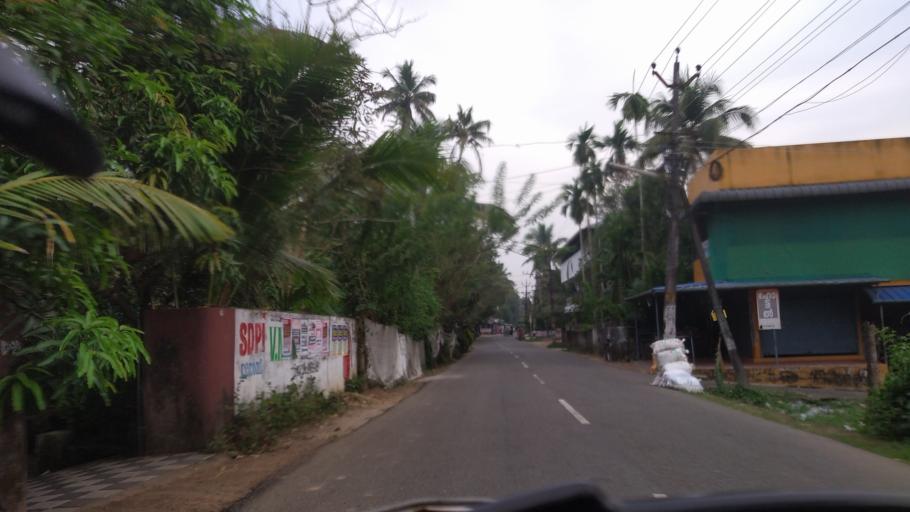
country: IN
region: Kerala
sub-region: Ernakulam
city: Elur
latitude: 10.1379
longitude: 76.2467
